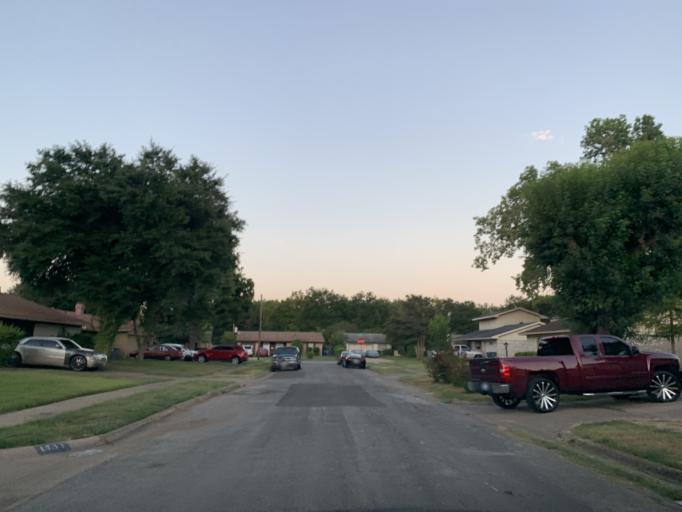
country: US
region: Texas
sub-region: Dallas County
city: Hutchins
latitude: 32.6732
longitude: -96.7941
